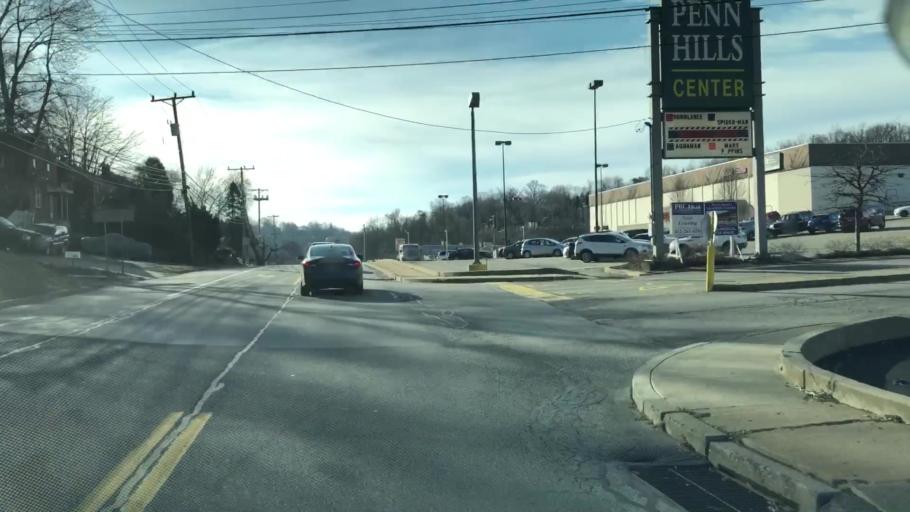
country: US
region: Pennsylvania
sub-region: Allegheny County
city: Churchill
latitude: 40.4630
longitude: -79.8241
